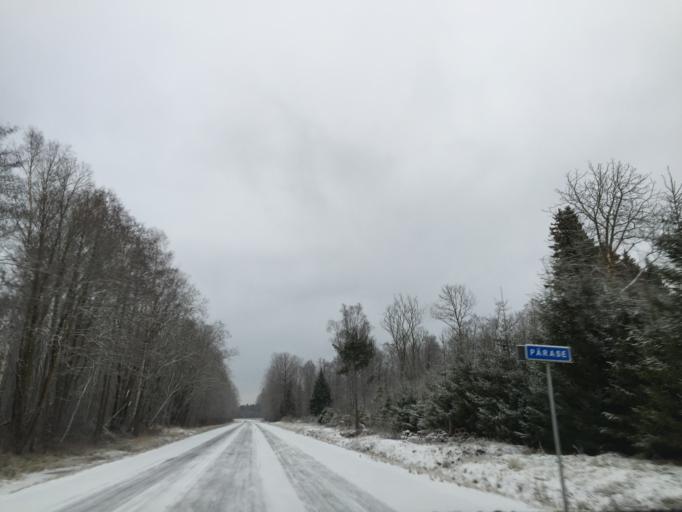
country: EE
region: Saare
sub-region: Orissaare vald
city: Orissaare
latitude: 58.6136
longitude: 23.3018
